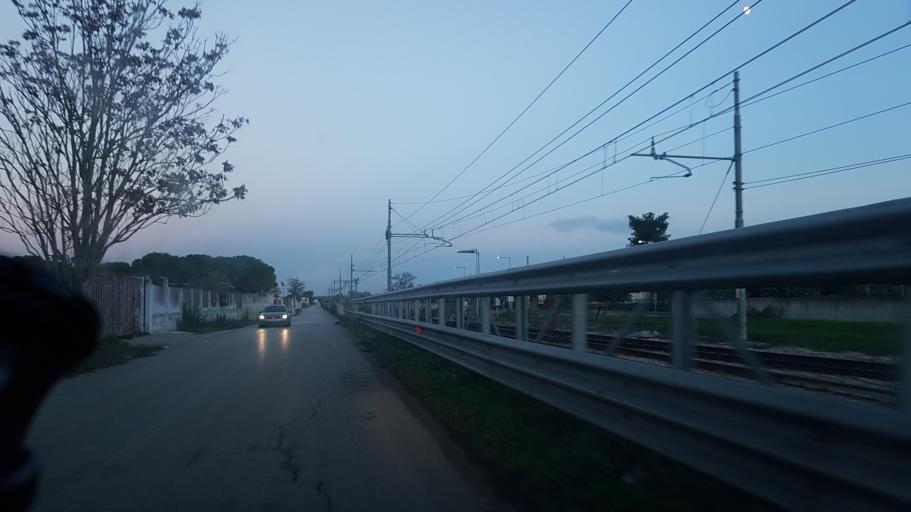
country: IT
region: Apulia
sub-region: Provincia di Brindisi
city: Latiano
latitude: 40.5584
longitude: 17.7210
